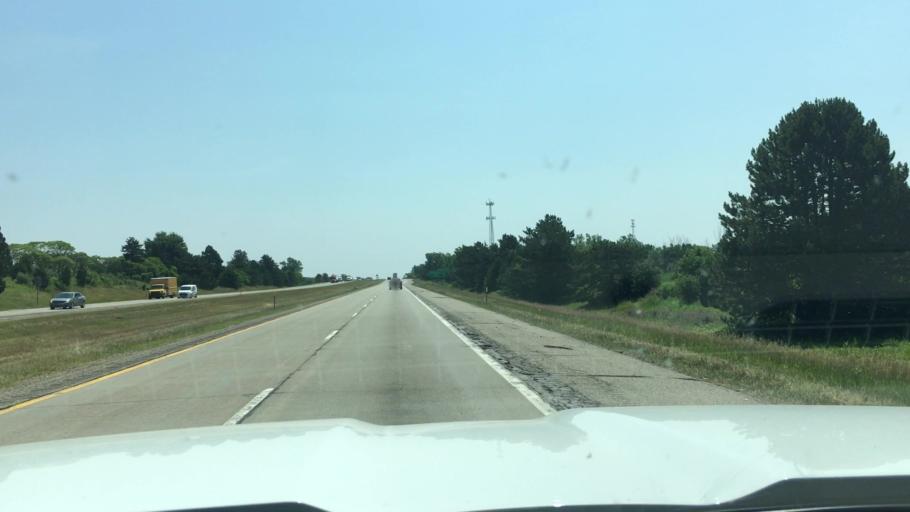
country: US
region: Michigan
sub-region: Eaton County
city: Grand Ledge
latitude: 42.8156
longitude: -84.7976
